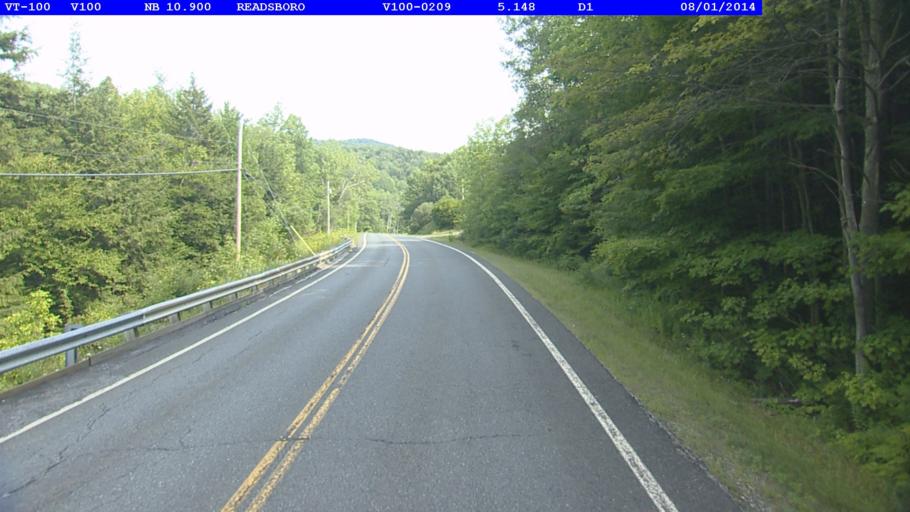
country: US
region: Massachusetts
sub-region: Berkshire County
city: North Adams
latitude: 42.7924
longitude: -72.9642
